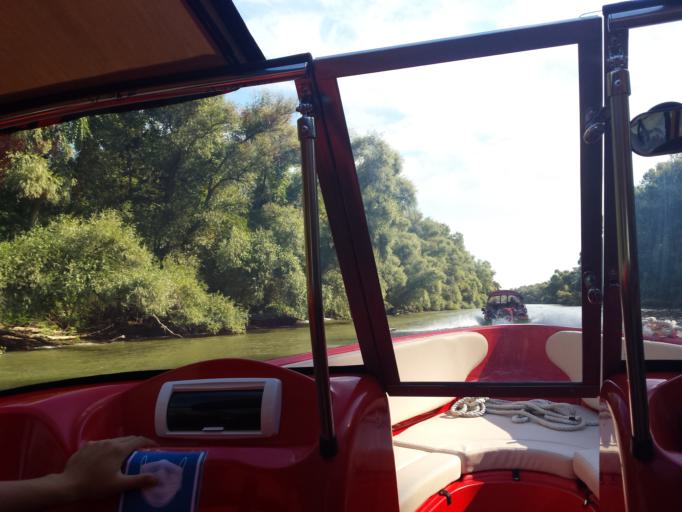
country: RO
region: Tulcea
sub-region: Comuna Nufaru
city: Malcoci
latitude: 45.2174
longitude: 28.8729
